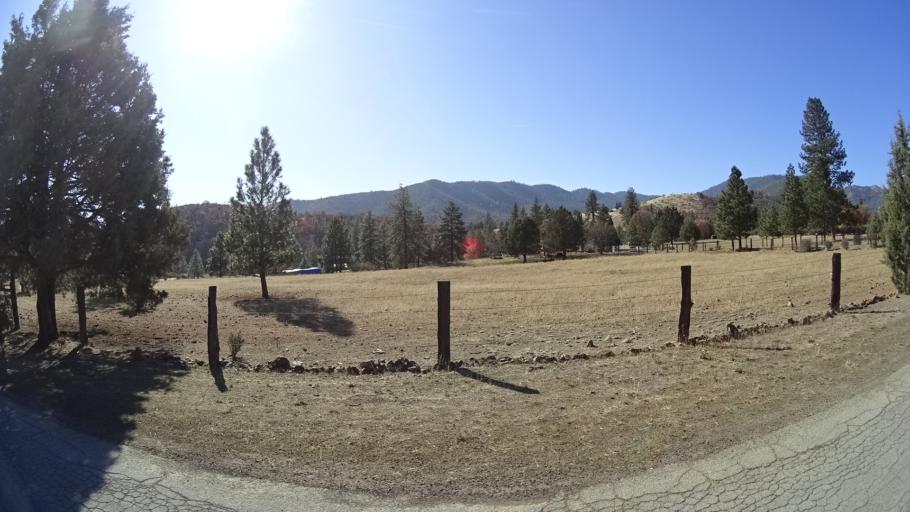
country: US
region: California
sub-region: Siskiyou County
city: Yreka
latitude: 41.7676
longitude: -122.6306
